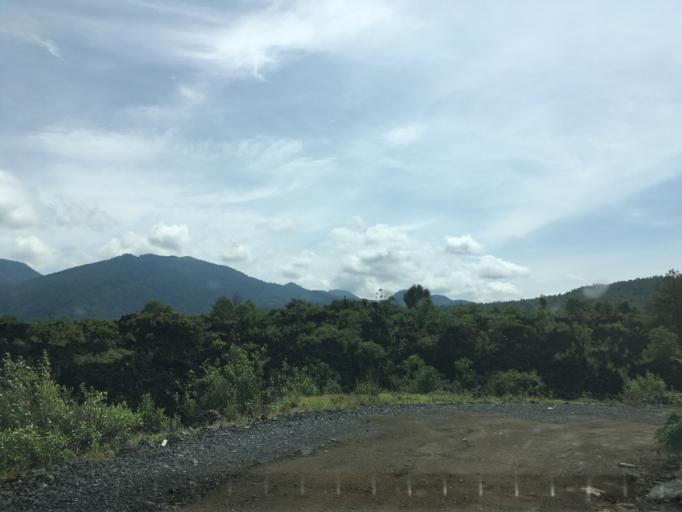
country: MX
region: Michoacan
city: Angahuan
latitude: 19.5220
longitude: -102.2270
